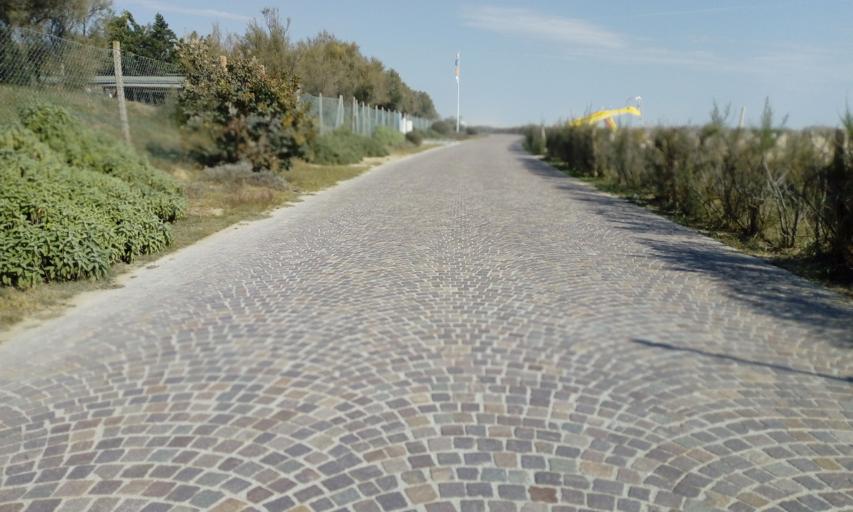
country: IT
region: Veneto
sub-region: Provincia di Venezia
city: Bibione
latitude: 45.6283
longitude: 13.0006
